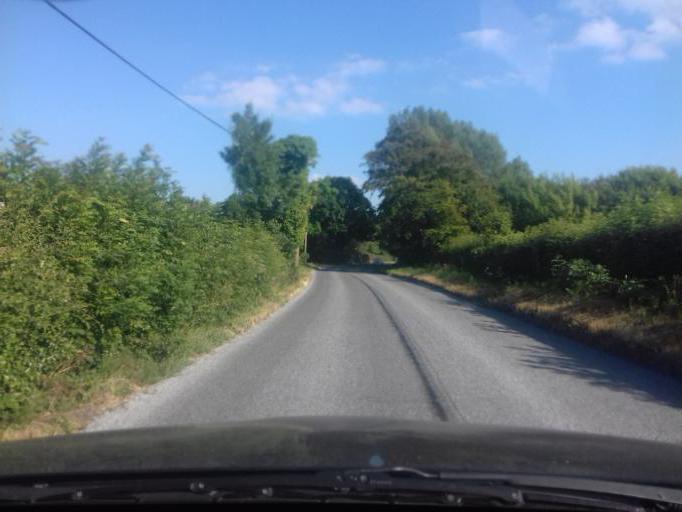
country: IE
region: Leinster
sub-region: Fingal County
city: Blanchardstown
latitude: 53.4486
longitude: -6.3927
